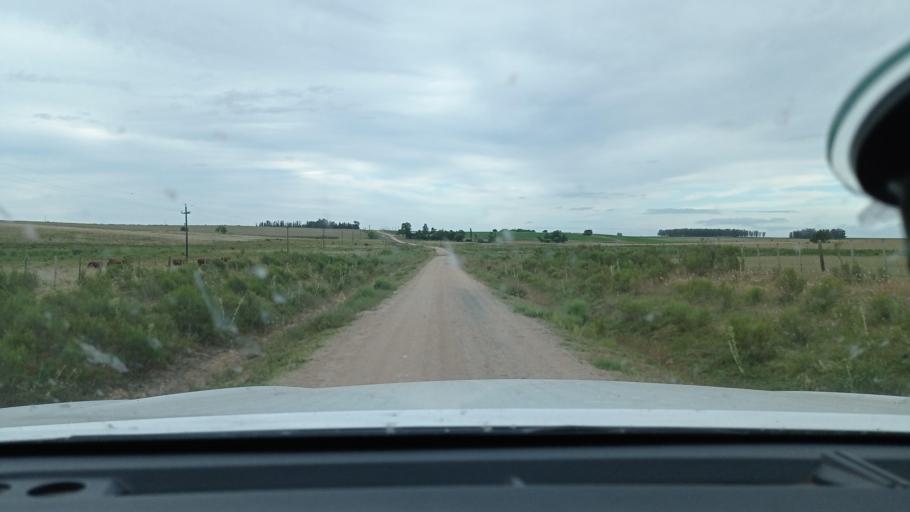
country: UY
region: Florida
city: Casupa
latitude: -34.1238
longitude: -55.7731
